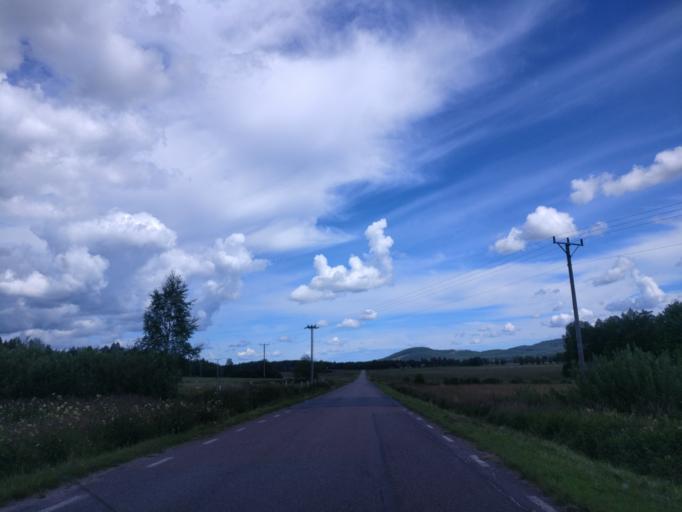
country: SE
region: Vaermland
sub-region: Hagfors Kommun
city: Ekshaerad
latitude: 60.1201
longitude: 13.4520
